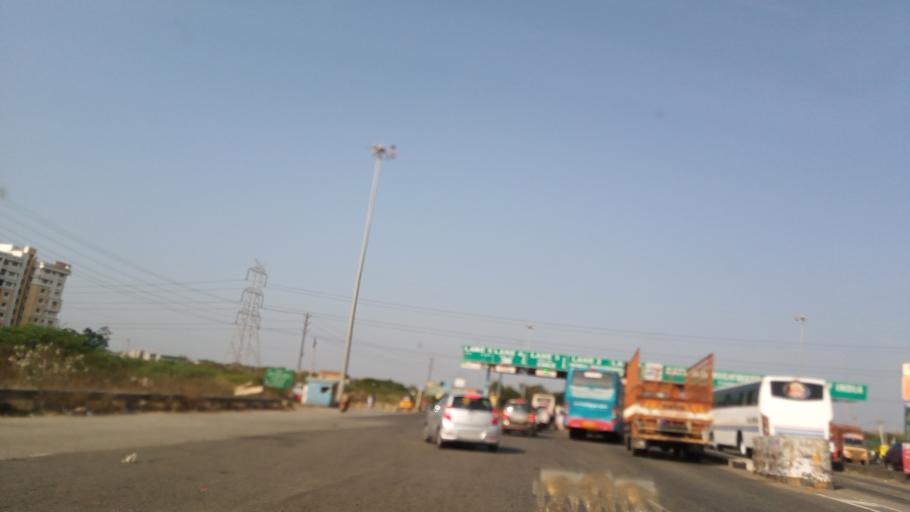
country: IN
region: Tamil Nadu
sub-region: Kancheepuram
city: Sriperumbudur
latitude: 12.9816
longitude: 79.9681
